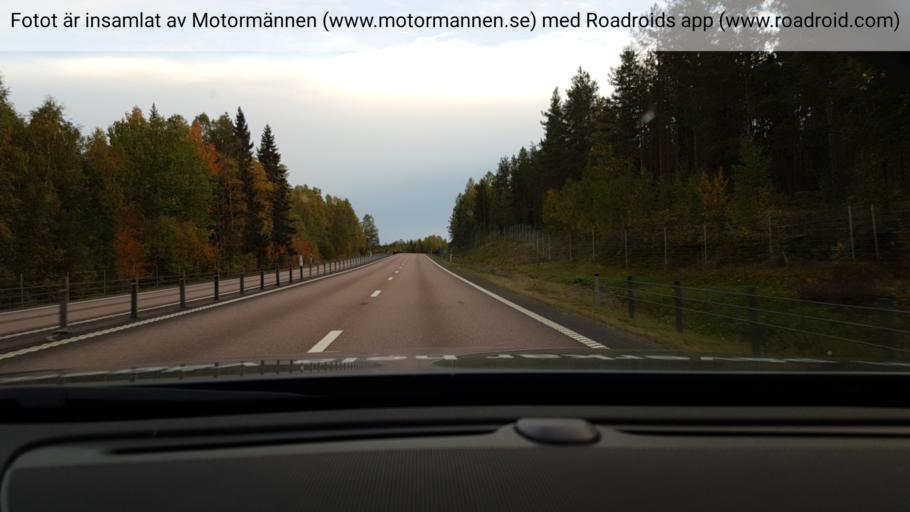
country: SE
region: Gaevleborg
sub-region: Hudiksvalls Kommun
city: Hudiksvall
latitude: 61.8651
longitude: 17.2043
